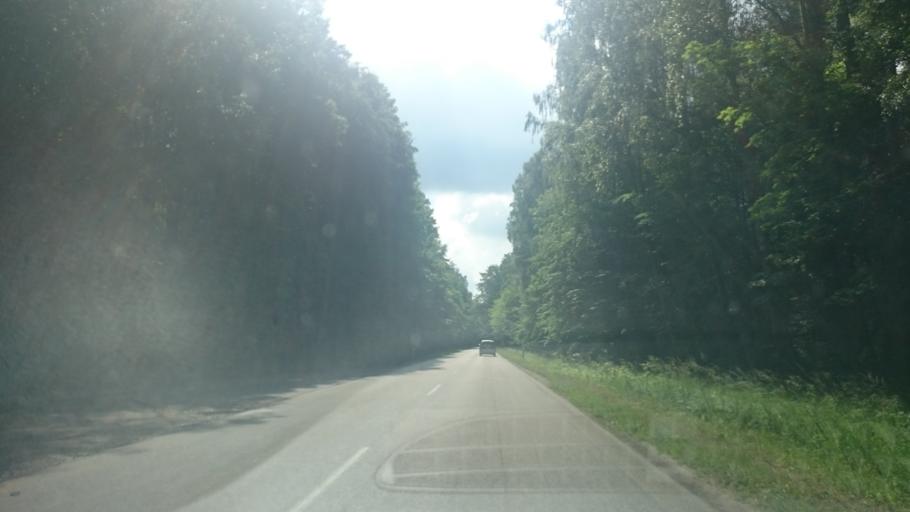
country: PL
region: Pomeranian Voivodeship
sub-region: Powiat starogardzki
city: Zblewo
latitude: 53.9638
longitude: 18.2884
